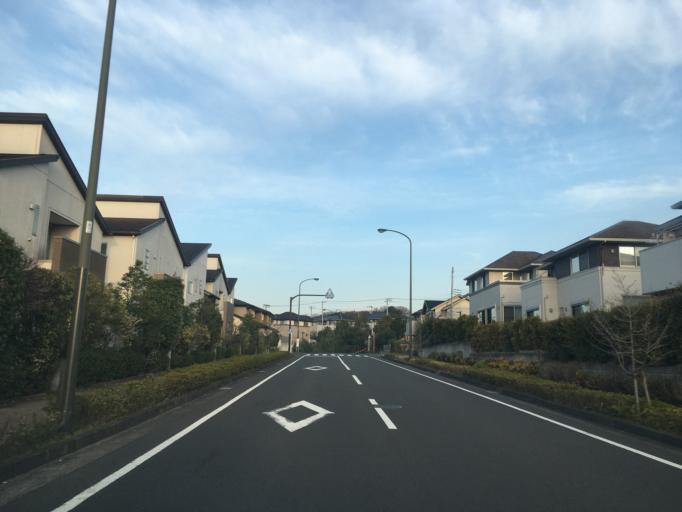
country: JP
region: Tokyo
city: Hino
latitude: 35.6301
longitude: 139.3942
